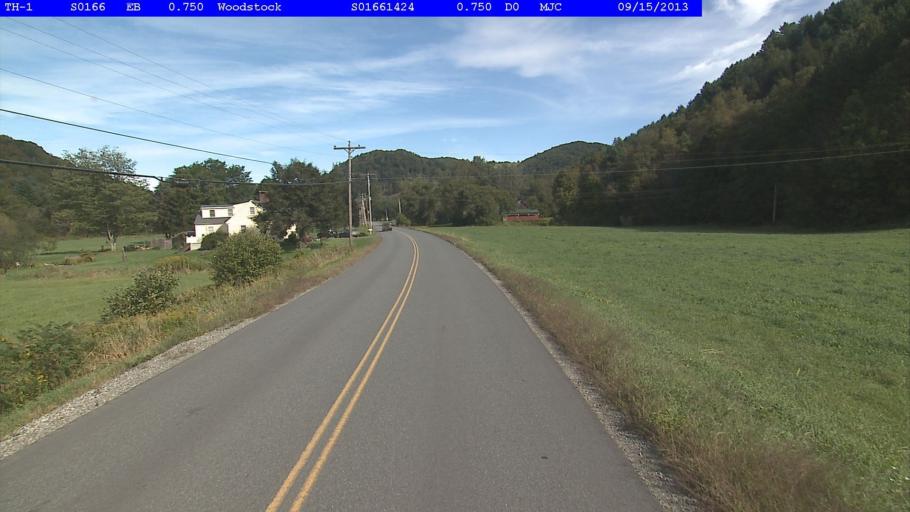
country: US
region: Vermont
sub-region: Windsor County
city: Woodstock
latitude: 43.6491
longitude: -72.5261
